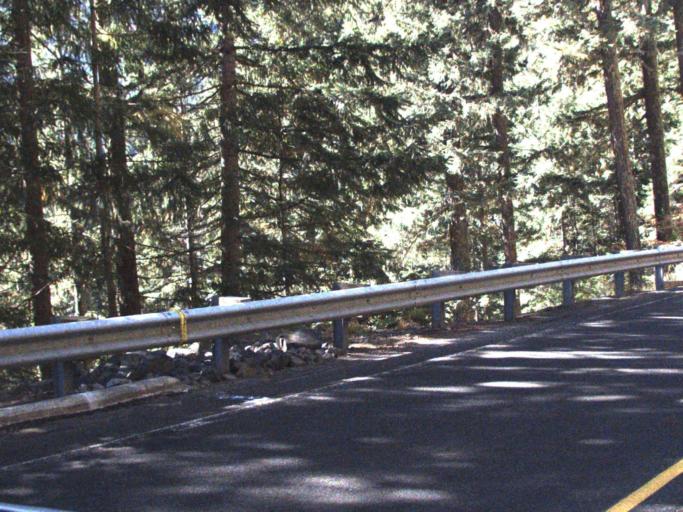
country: US
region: Washington
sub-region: Pierce County
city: Buckley
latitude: 46.6719
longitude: -121.5115
